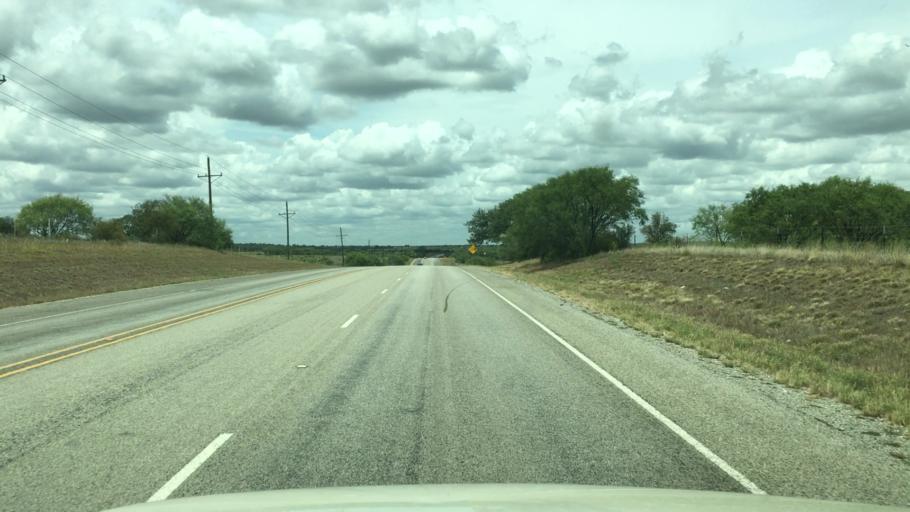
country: US
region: Texas
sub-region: McCulloch County
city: Brady
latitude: 31.0026
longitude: -99.1819
